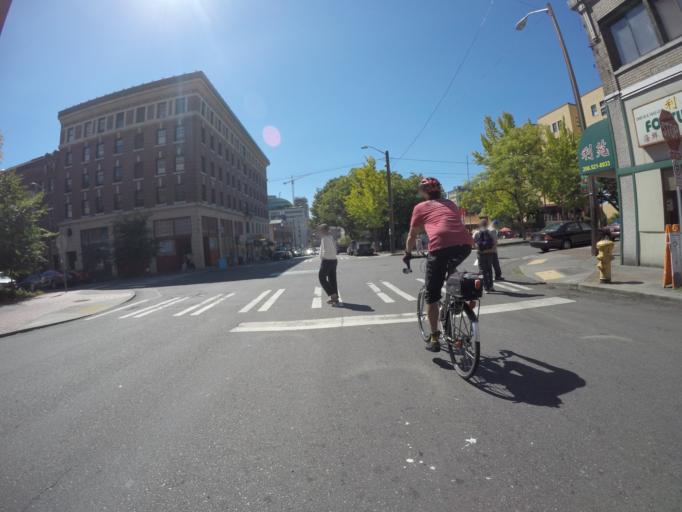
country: US
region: Washington
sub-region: King County
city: Seattle
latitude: 47.5985
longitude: -122.3249
